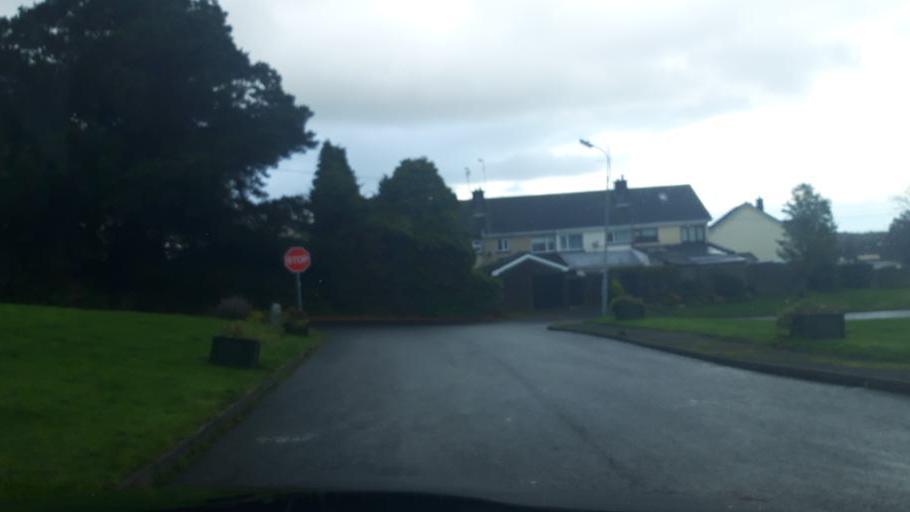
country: IE
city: Newtownmountkennedy
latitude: 53.0874
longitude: -6.1124
